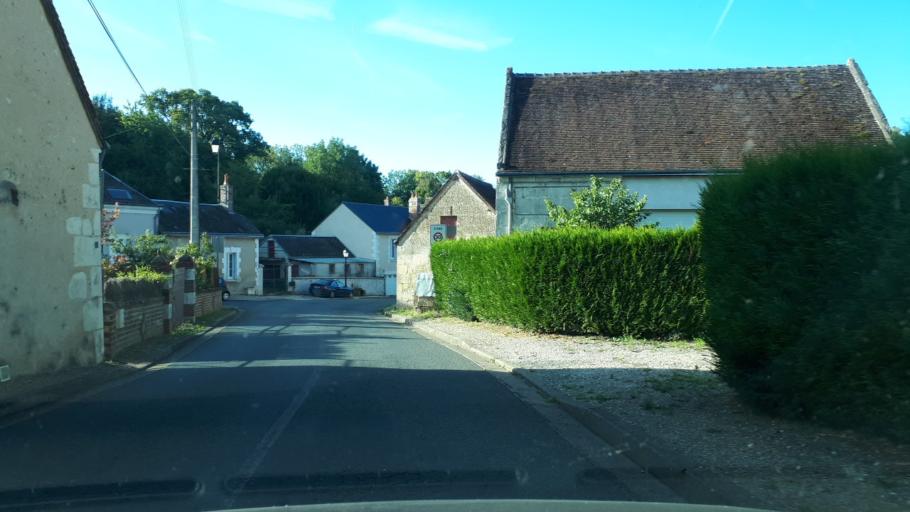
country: FR
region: Centre
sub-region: Departement du Loir-et-Cher
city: Lunay
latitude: 47.7529
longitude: 0.9390
